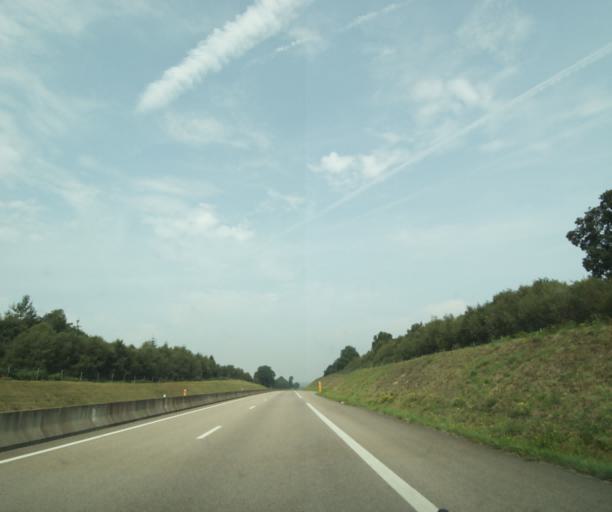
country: FR
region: Lower Normandy
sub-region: Departement du Calvados
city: Falaise
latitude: 48.8445
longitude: -0.1673
